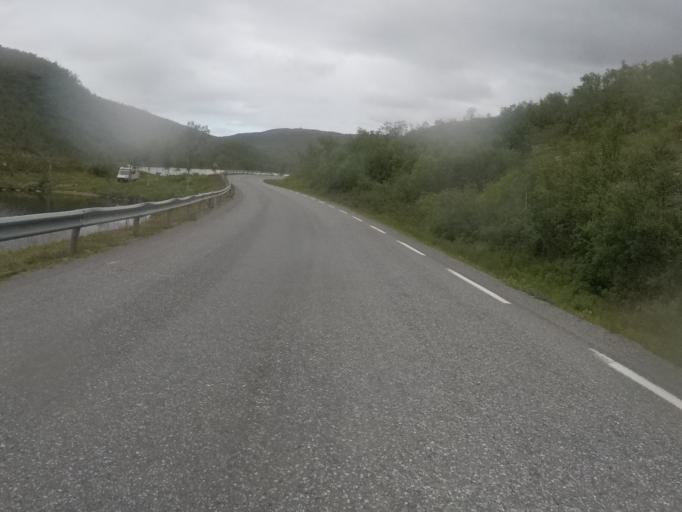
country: NO
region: Finnmark Fylke
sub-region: Alta
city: Alta
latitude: 69.7399
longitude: 23.3869
